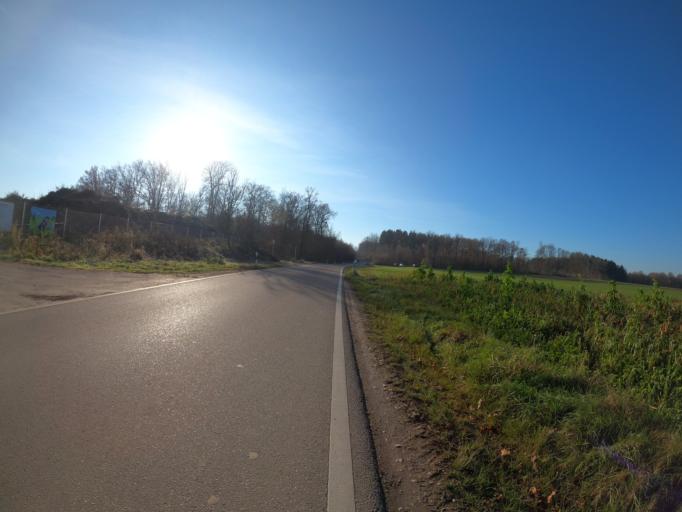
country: DE
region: Baden-Wuerttemberg
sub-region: Regierungsbezirk Stuttgart
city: Ebersbach an der Fils
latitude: 48.7021
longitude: 9.5411
